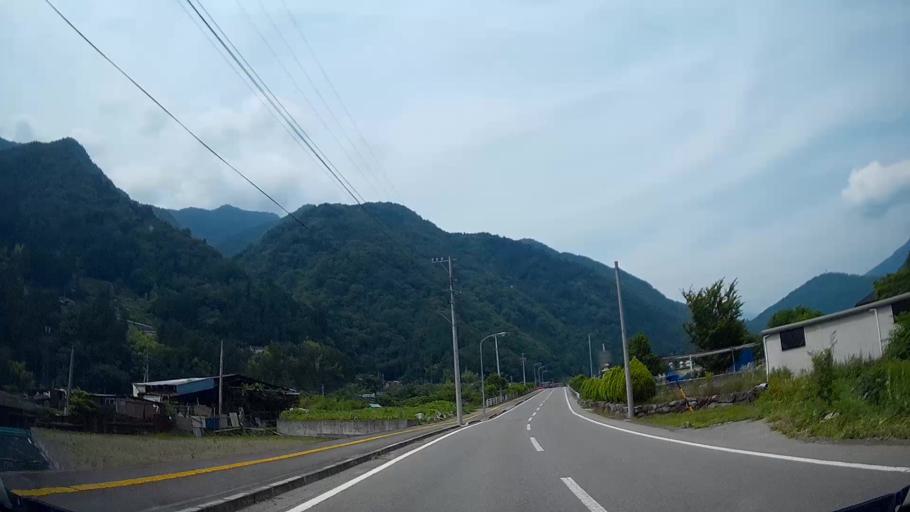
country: JP
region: Nagano
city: Iida
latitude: 35.3172
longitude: 137.9269
